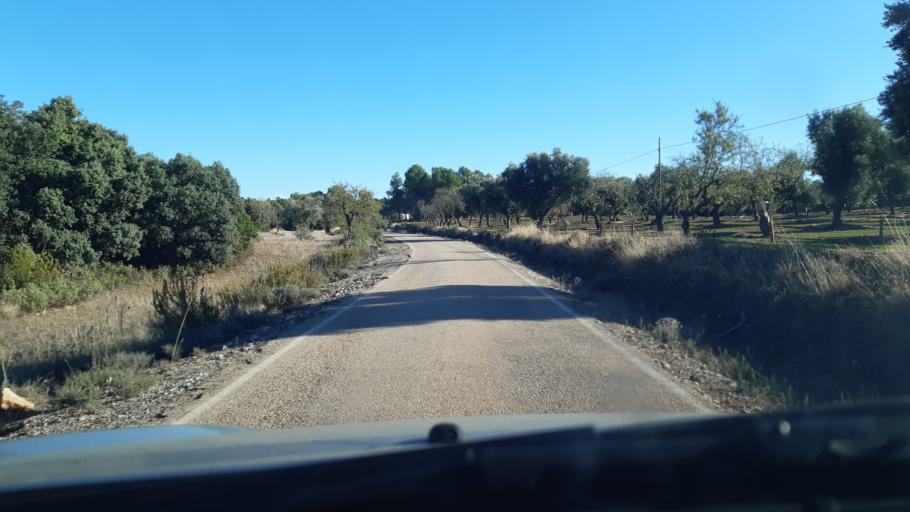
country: ES
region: Aragon
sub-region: Provincia de Teruel
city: Fornoles
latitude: 40.9134
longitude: -0.0193
